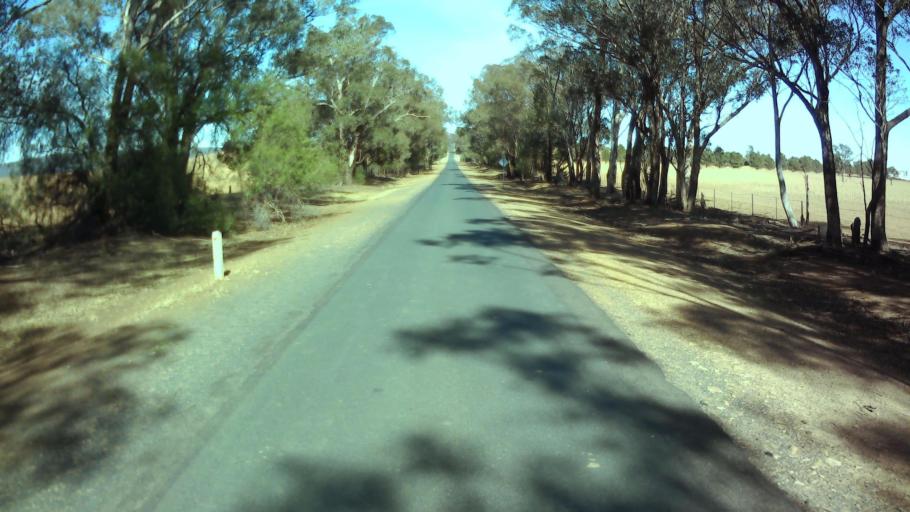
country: AU
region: New South Wales
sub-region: Weddin
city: Grenfell
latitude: -33.9070
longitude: 148.0736
